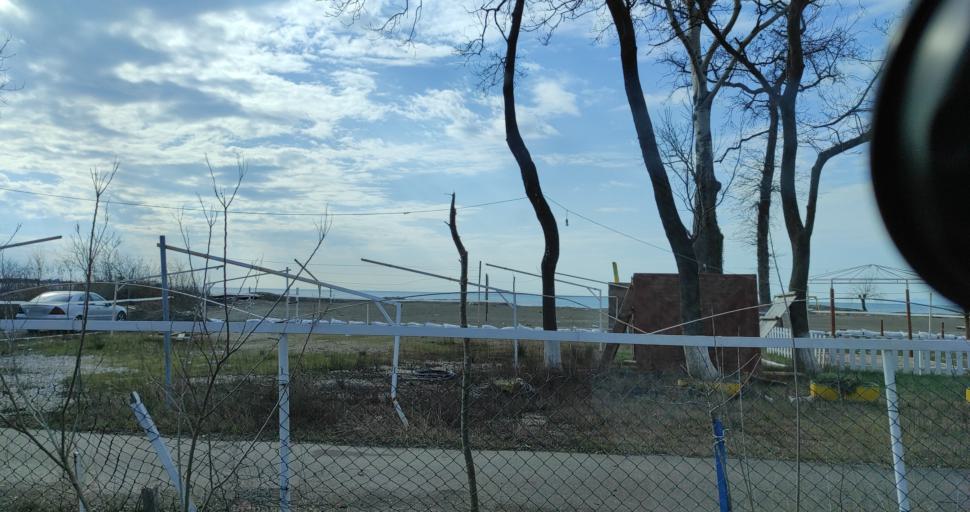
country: AL
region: Lezhe
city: Shengjin
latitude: 41.7777
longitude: 19.6032
